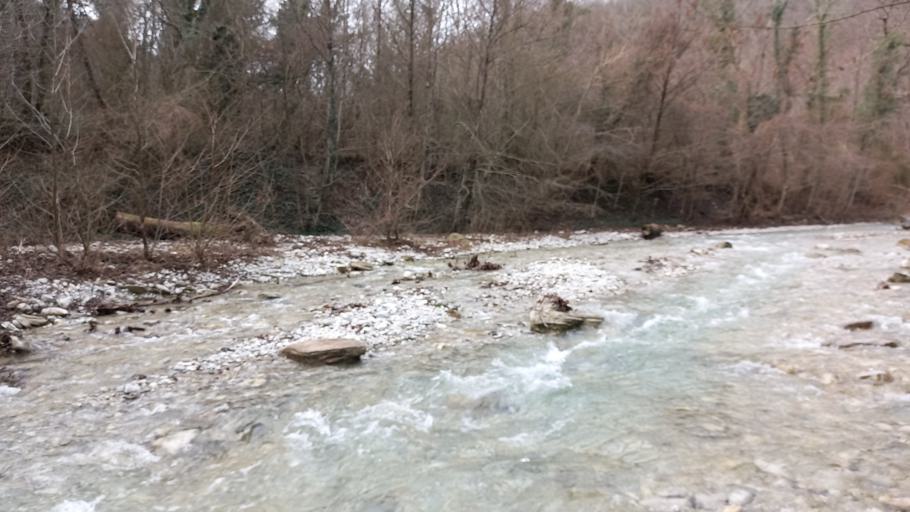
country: RU
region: Krasnodarskiy
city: Dzhubga
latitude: 44.4089
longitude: 38.7158
